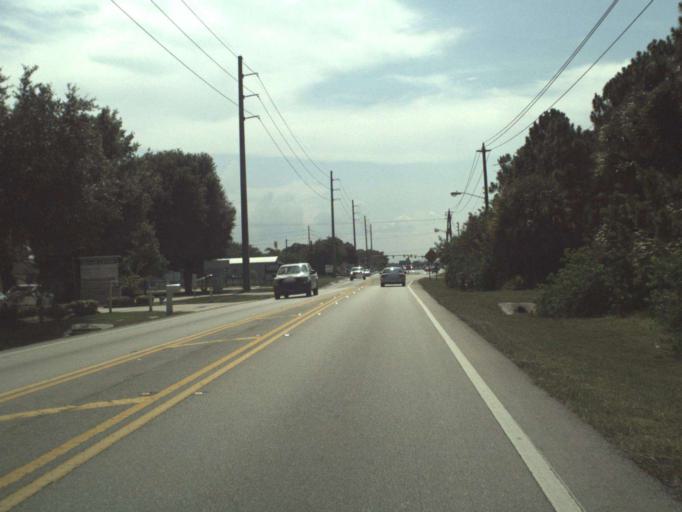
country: US
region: Florida
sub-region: Brevard County
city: Palm Bay
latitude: 27.9984
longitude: -80.6171
